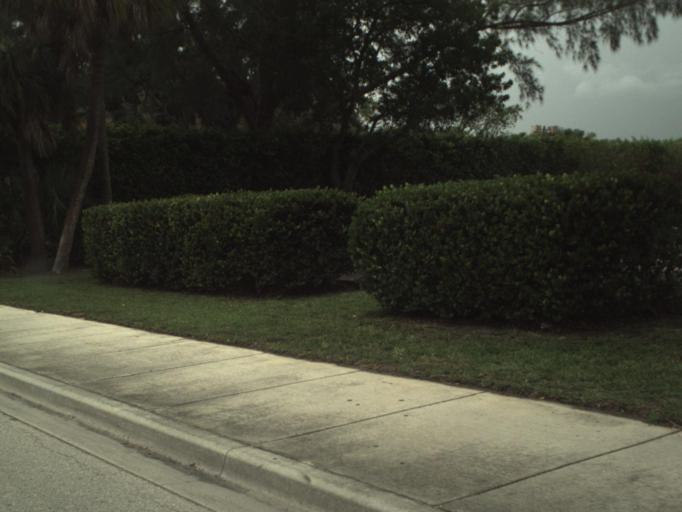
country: US
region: Florida
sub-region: Palm Beach County
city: Royal Palm Estates
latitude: 26.6730
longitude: -80.1124
